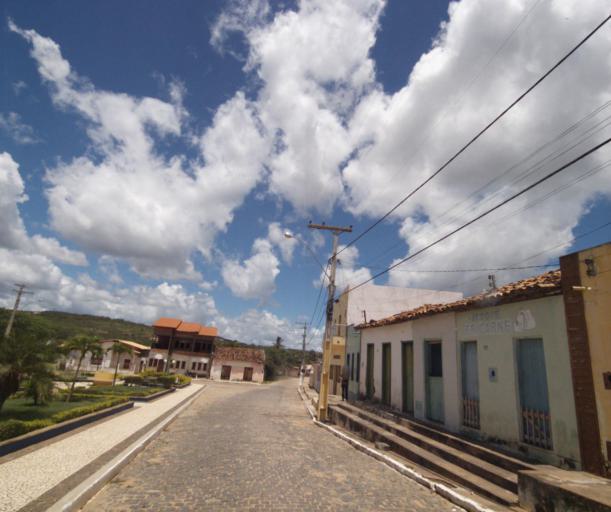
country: BR
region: Bahia
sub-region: Pocoes
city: Pocoes
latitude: -14.3753
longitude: -40.5042
